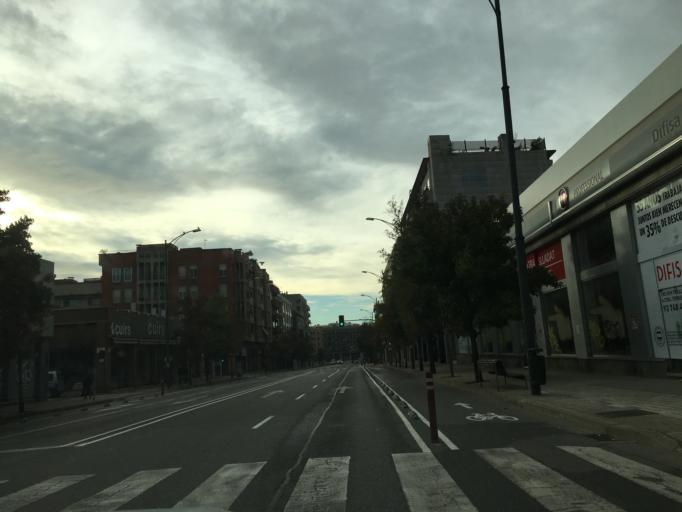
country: ES
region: Catalonia
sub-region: Provincia de Barcelona
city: Sabadell
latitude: 41.5469
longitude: 2.0992
